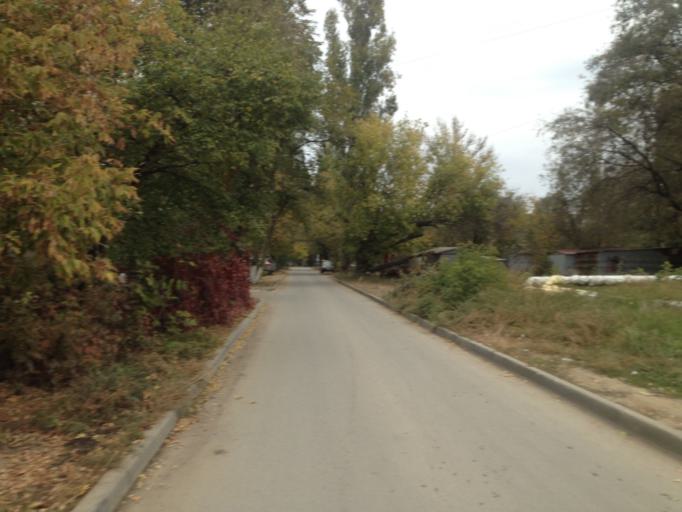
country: RU
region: Volgograd
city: Volgograd
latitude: 48.7363
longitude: 44.4888
